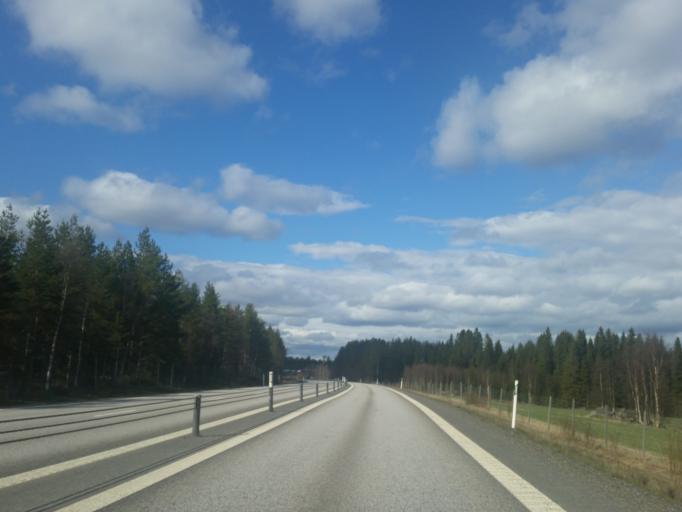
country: SE
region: Vaesterbotten
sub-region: Robertsfors Kommun
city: Robertsfors
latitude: 64.1101
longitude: 20.8785
